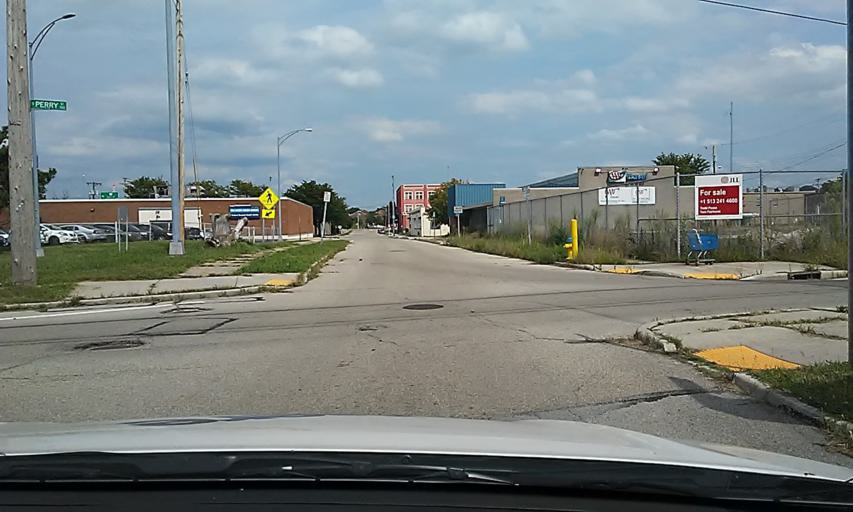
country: US
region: Ohio
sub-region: Montgomery County
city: Dayton
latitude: 39.7502
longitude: -84.1935
